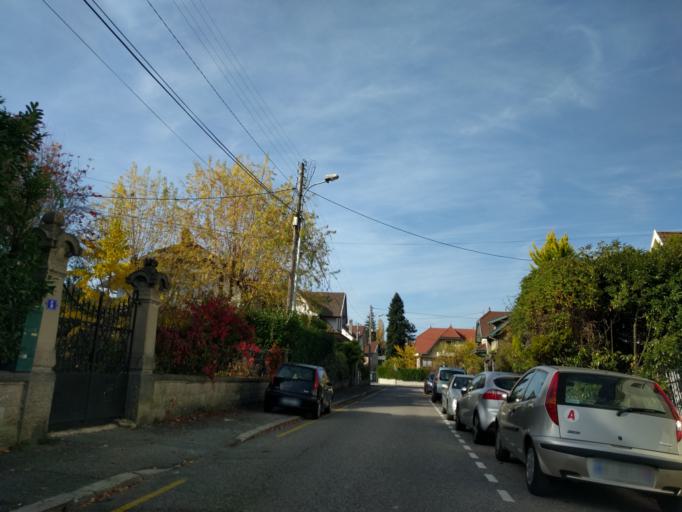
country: FR
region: Rhone-Alpes
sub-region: Departement de la Haute-Savoie
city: Annecy
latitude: 45.9095
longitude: 6.1292
